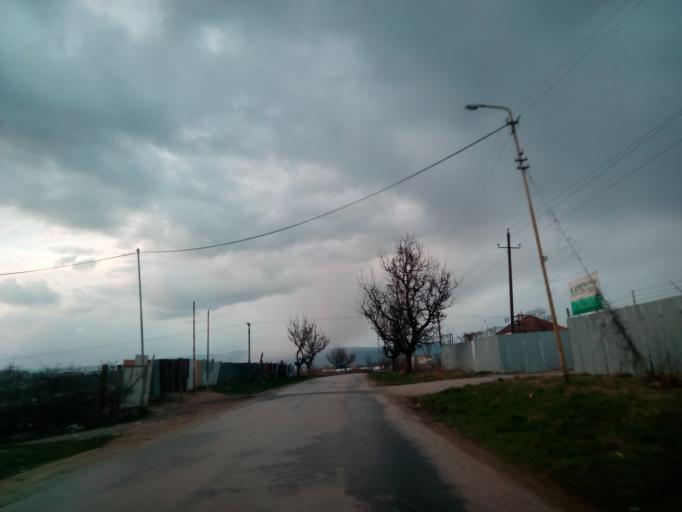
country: SK
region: Kosicky
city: Moldava nad Bodvou
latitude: 48.5992
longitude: 20.9972
